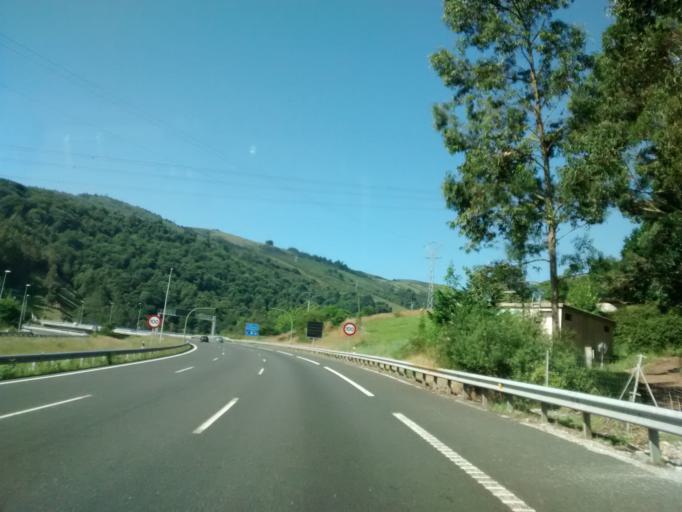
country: ES
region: Cantabria
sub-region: Provincia de Cantabria
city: Cartes
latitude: 43.3101
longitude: -4.0771
